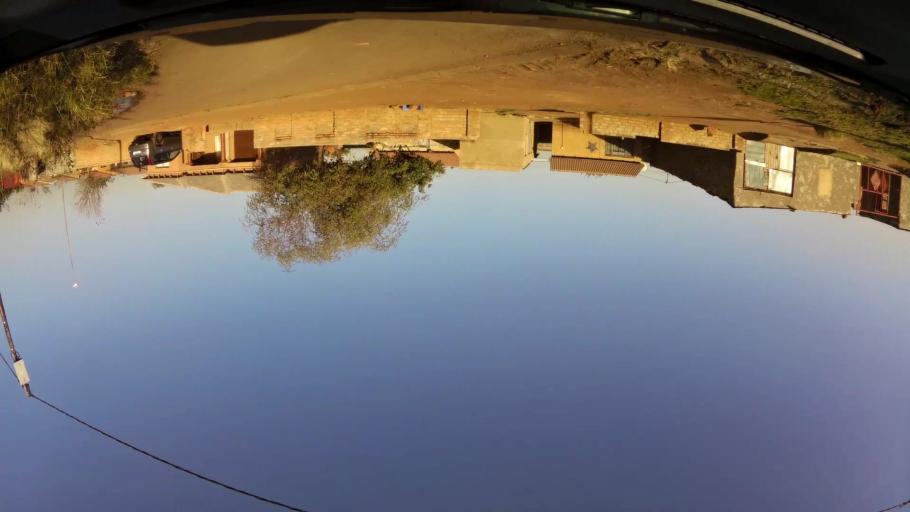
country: ZA
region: Gauteng
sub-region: City of Tshwane Metropolitan Municipality
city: Mabopane
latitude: -25.5952
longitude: 28.1030
